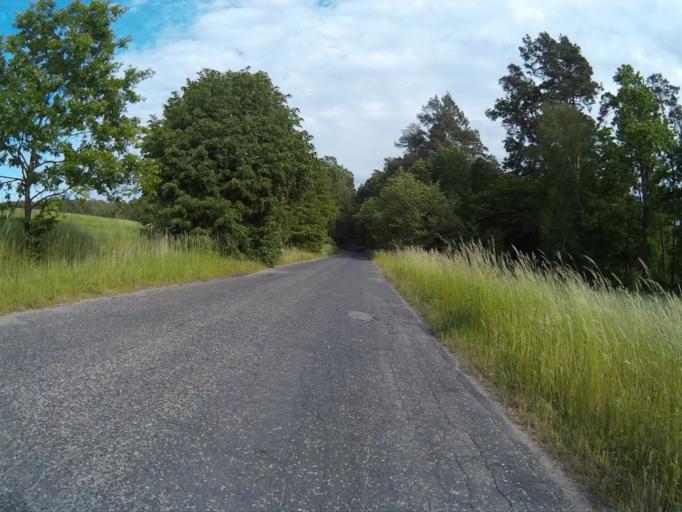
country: PL
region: Kujawsko-Pomorskie
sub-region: Powiat tucholski
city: Lubiewo
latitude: 53.4776
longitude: 17.9636
